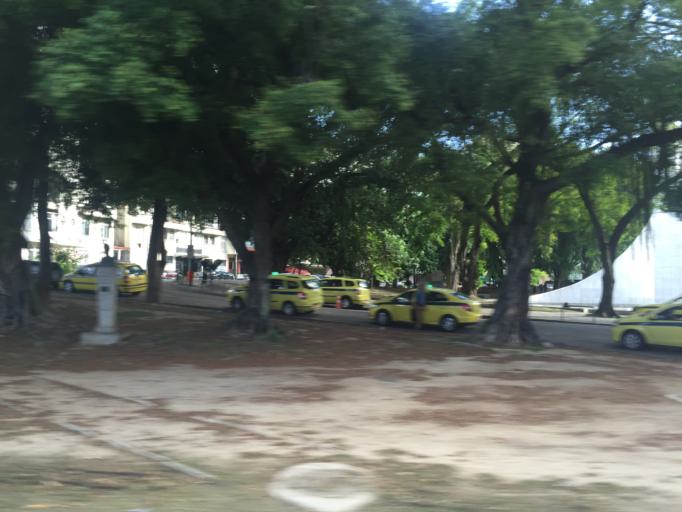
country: BR
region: Rio de Janeiro
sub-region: Rio De Janeiro
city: Rio de Janeiro
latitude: -22.9218
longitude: -43.1729
